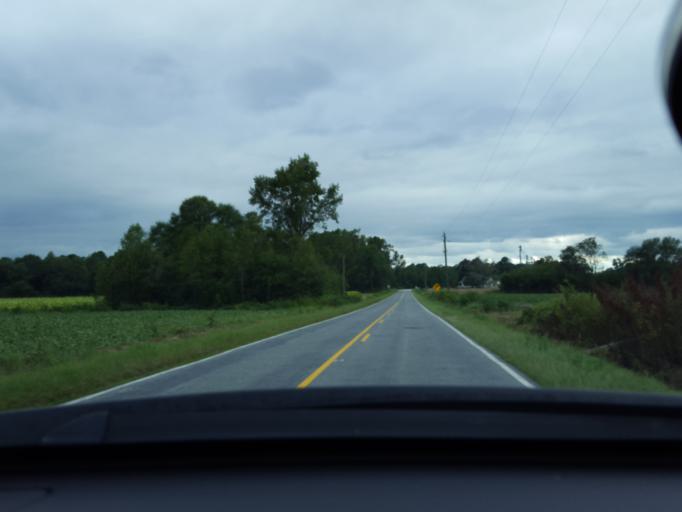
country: US
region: North Carolina
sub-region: Sampson County
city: Roseboro
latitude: 34.7852
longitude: -78.3797
